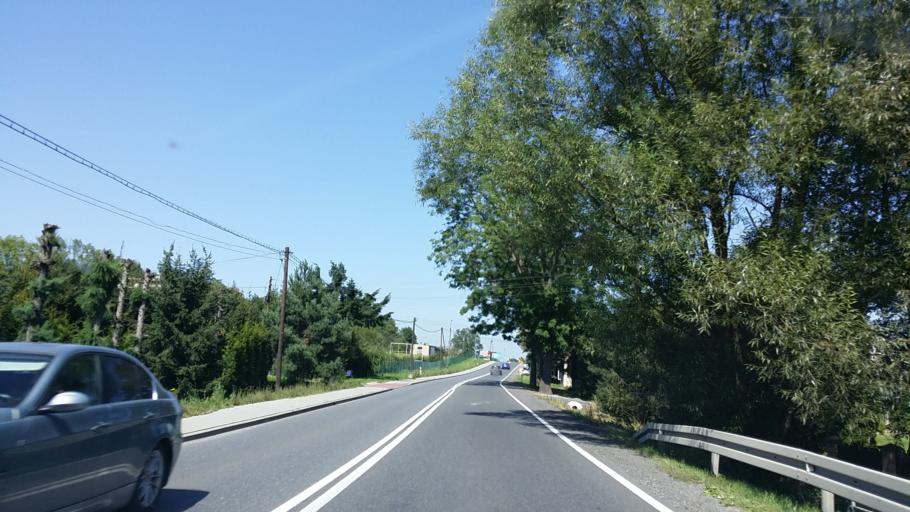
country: PL
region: Lesser Poland Voivodeship
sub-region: Powiat wadowicki
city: Radocza
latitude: 49.9110
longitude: 19.4835
